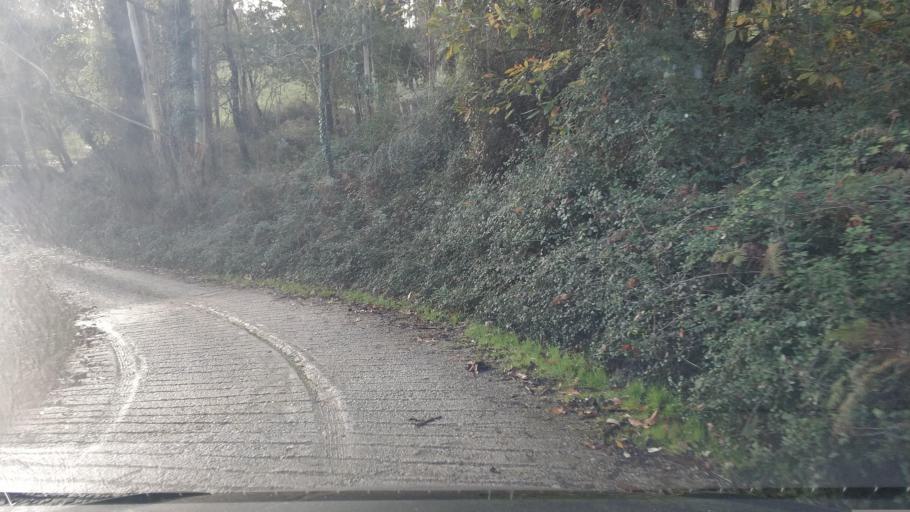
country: ES
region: Cantabria
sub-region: Provincia de Cantabria
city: Luzmela
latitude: 43.3387
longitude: -4.1862
